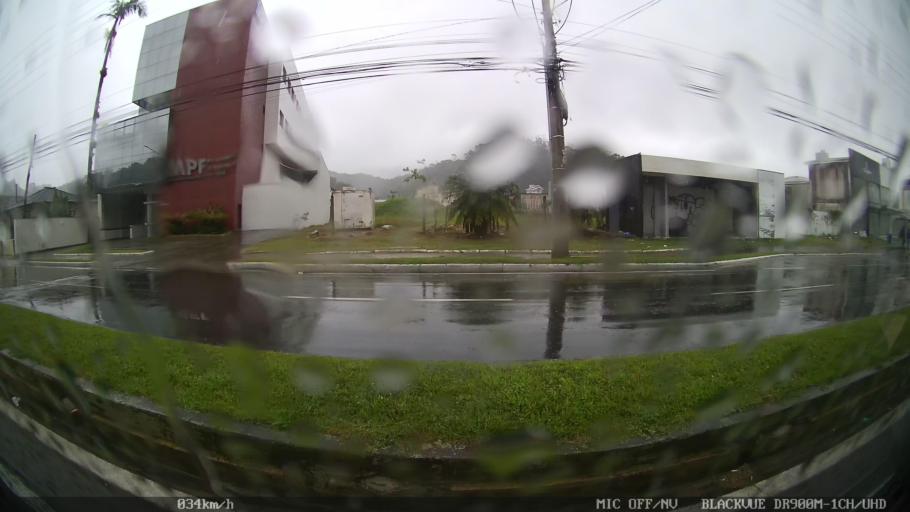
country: BR
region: Santa Catarina
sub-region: Itajai
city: Itajai
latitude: -26.9301
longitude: -48.6447
